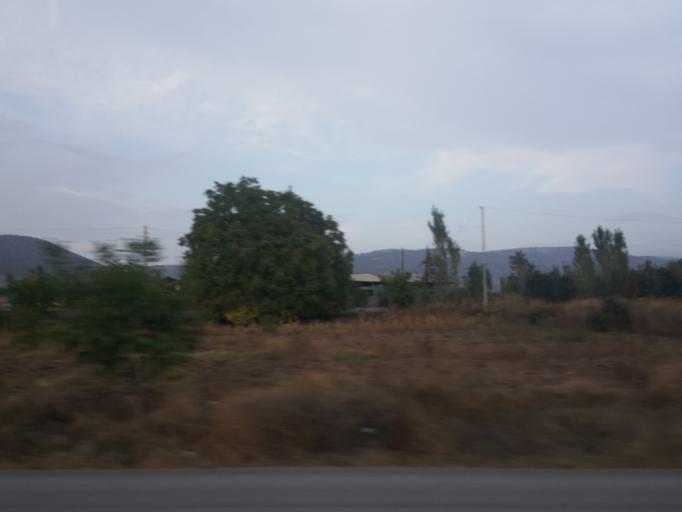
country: TR
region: Amasya
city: Gumushacikoy
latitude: 40.8772
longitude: 35.2317
